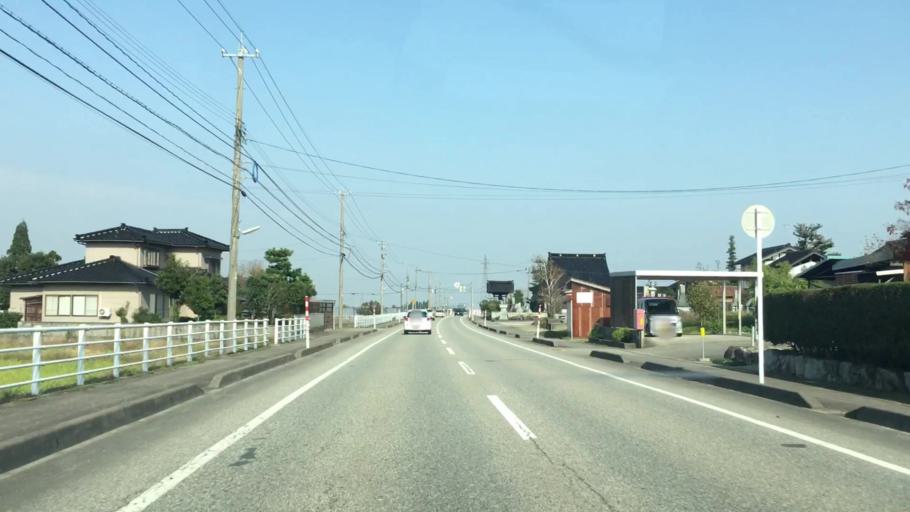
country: JP
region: Toyama
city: Yatsuomachi-higashikumisaka
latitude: 36.6013
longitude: 137.1915
